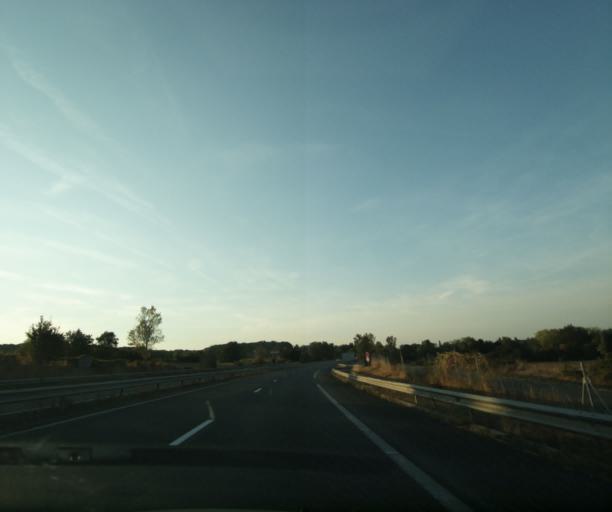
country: FR
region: Aquitaine
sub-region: Departement du Lot-et-Garonne
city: Boe
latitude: 44.1486
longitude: 0.6218
